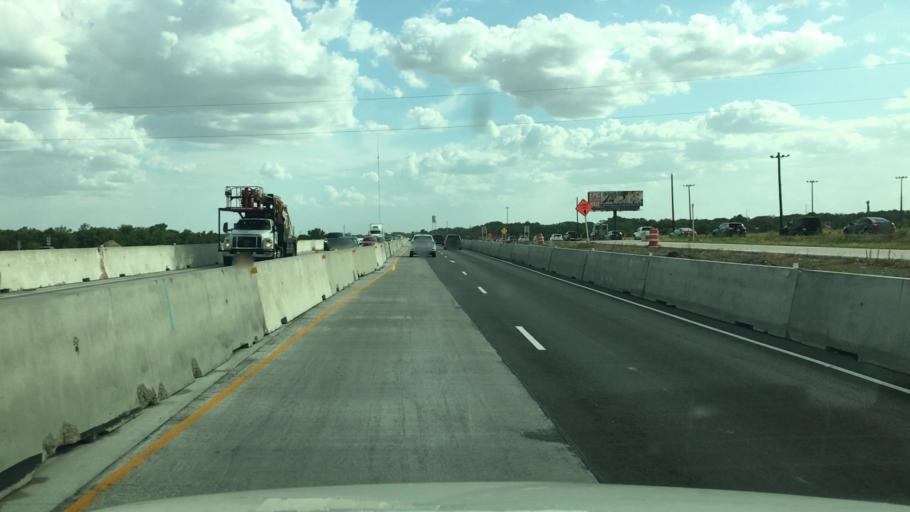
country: US
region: Texas
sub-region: McLennan County
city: Bruceville-Eddy
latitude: 31.3027
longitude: -97.2477
